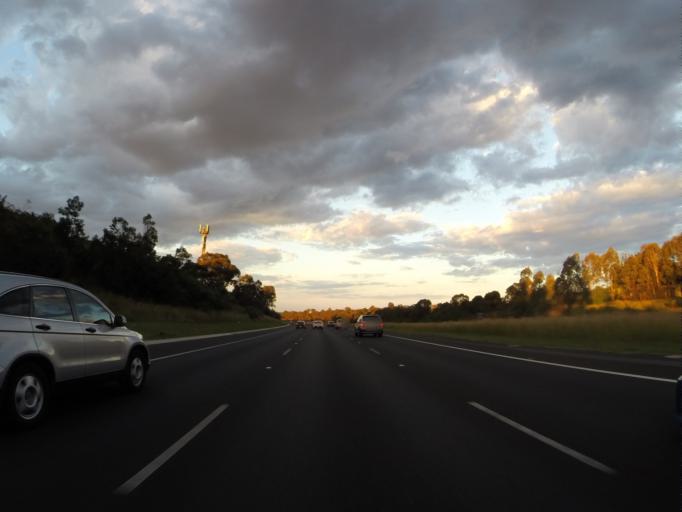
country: AU
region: New South Wales
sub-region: Campbelltown Municipality
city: Campbelltown
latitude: -34.0521
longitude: 150.8103
